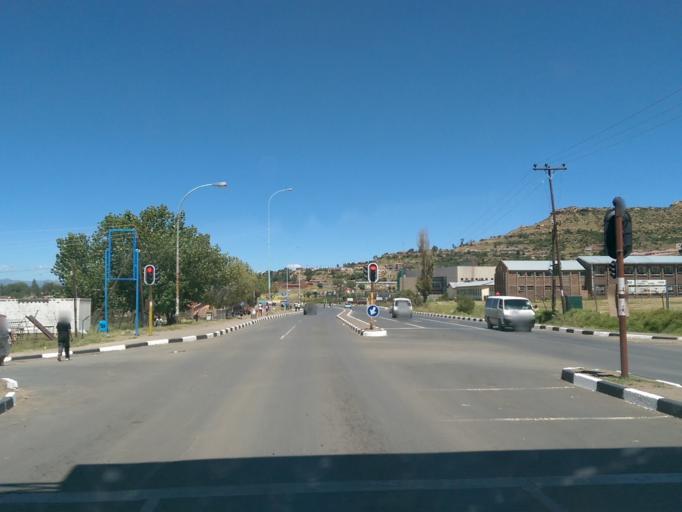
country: LS
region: Maseru
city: Maseru
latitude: -29.3200
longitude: 27.4968
